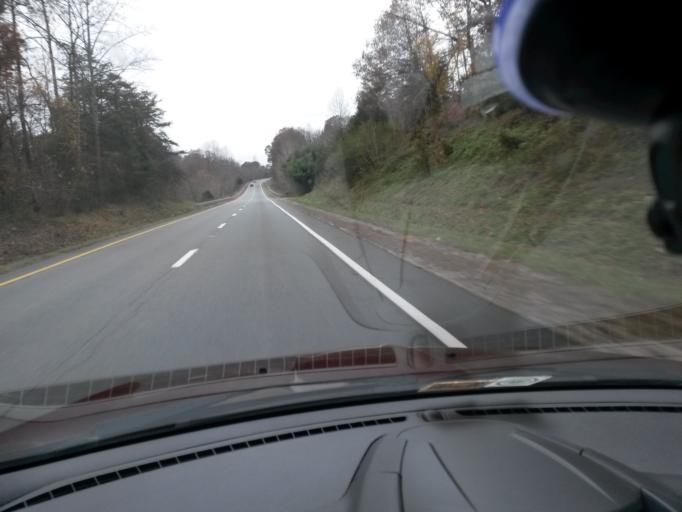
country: US
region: Virginia
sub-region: Nelson County
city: Nellysford
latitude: 37.8433
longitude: -78.7797
